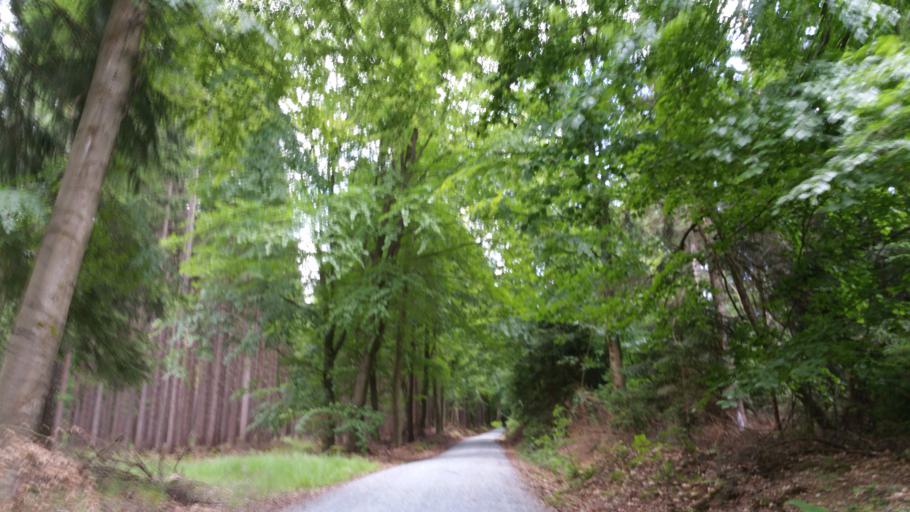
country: DE
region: Bavaria
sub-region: Upper Franconia
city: Kirchenlamitz
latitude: 50.1778
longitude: 11.9285
